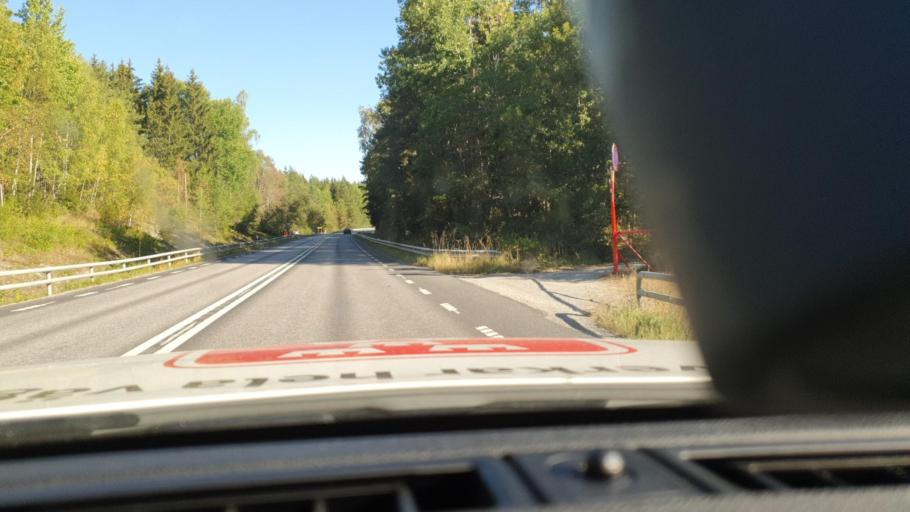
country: SE
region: Stockholm
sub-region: Lidingo
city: Brevik
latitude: 59.4323
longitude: 18.2199
